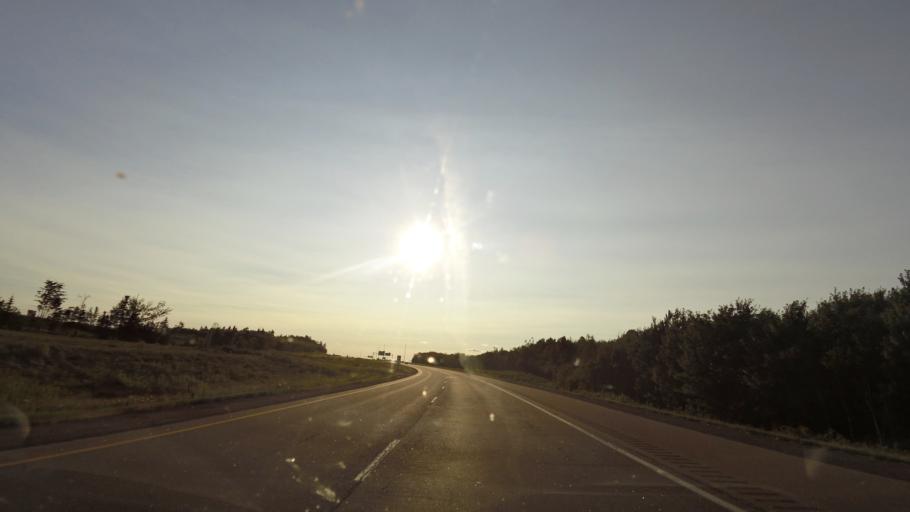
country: CA
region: New Brunswick
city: Dieppe
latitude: 46.1305
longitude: -64.6630
